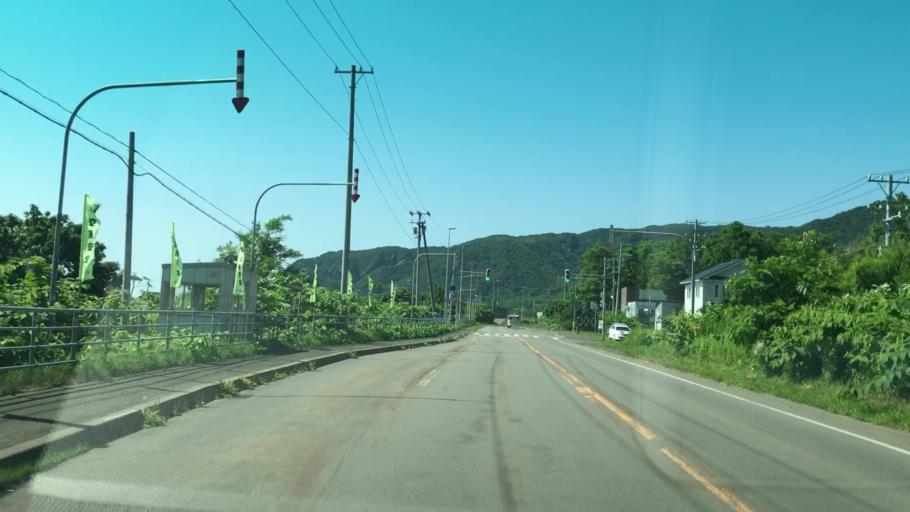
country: JP
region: Hokkaido
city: Iwanai
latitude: 43.0702
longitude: 140.4915
